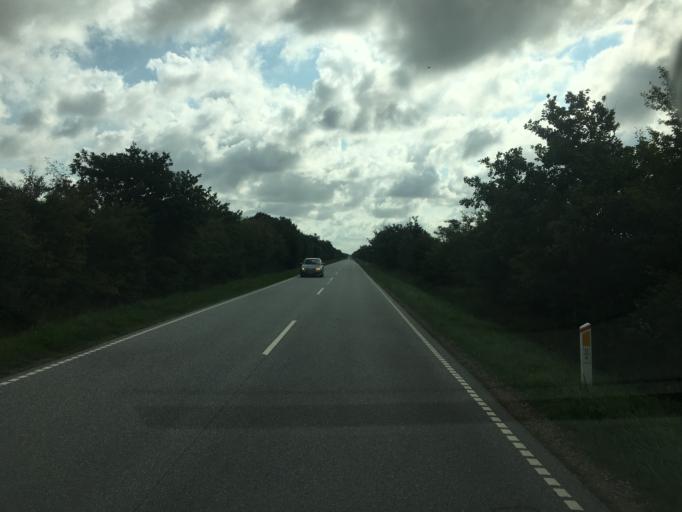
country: DK
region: South Denmark
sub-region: Tonder Kommune
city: Sherrebek
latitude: 55.1256
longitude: 8.8134
